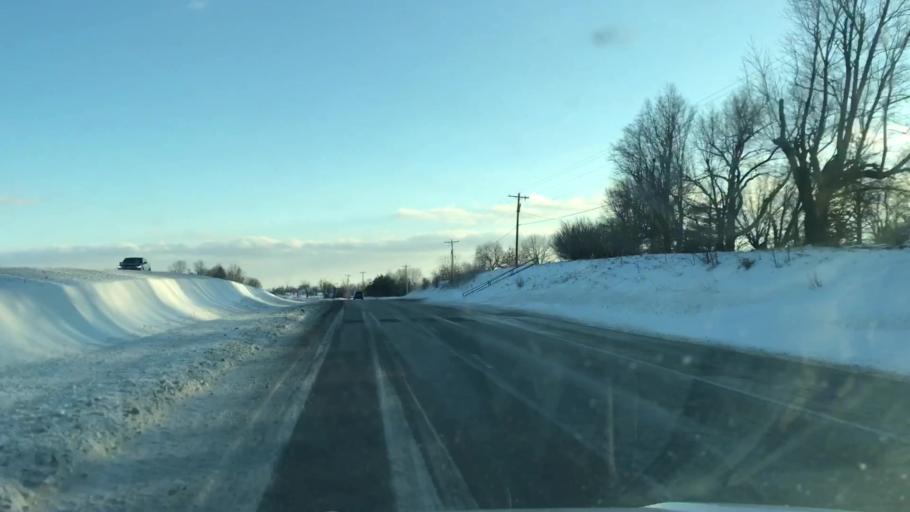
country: US
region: Missouri
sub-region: Andrew County
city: Country Club Village
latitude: 39.8787
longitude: -94.8091
